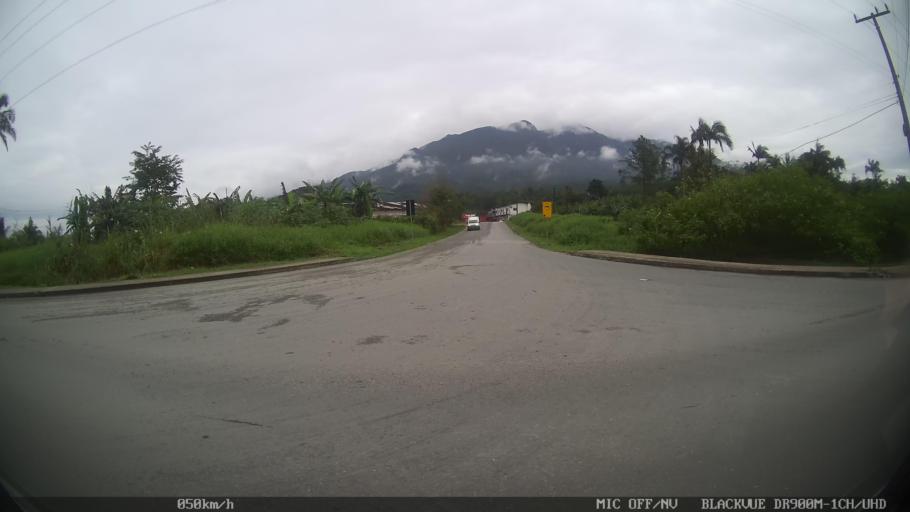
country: BR
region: Santa Catarina
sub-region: Joinville
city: Joinville
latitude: -26.0646
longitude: -48.8571
